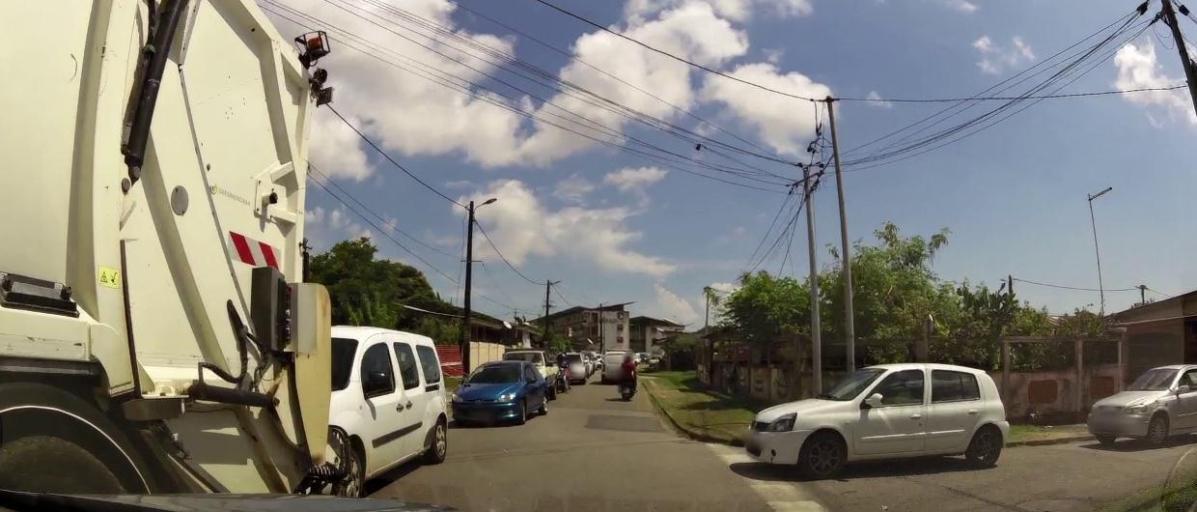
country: GF
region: Guyane
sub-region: Guyane
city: Cayenne
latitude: 4.9227
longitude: -52.3195
